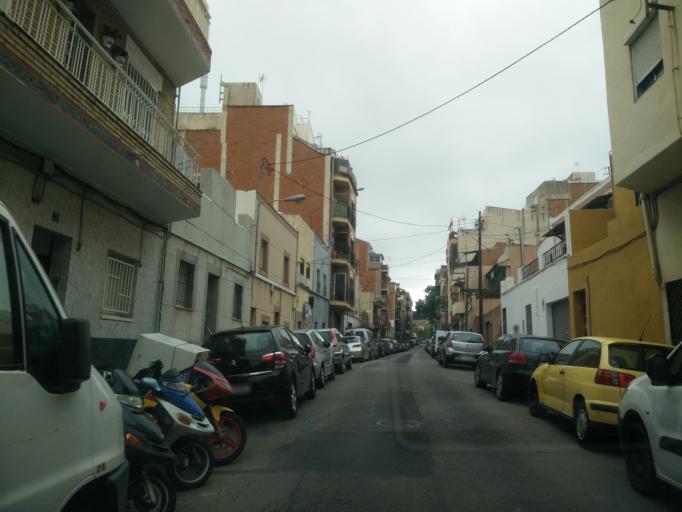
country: ES
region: Catalonia
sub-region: Provincia de Barcelona
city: Llefia
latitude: 41.4484
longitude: 2.2281
